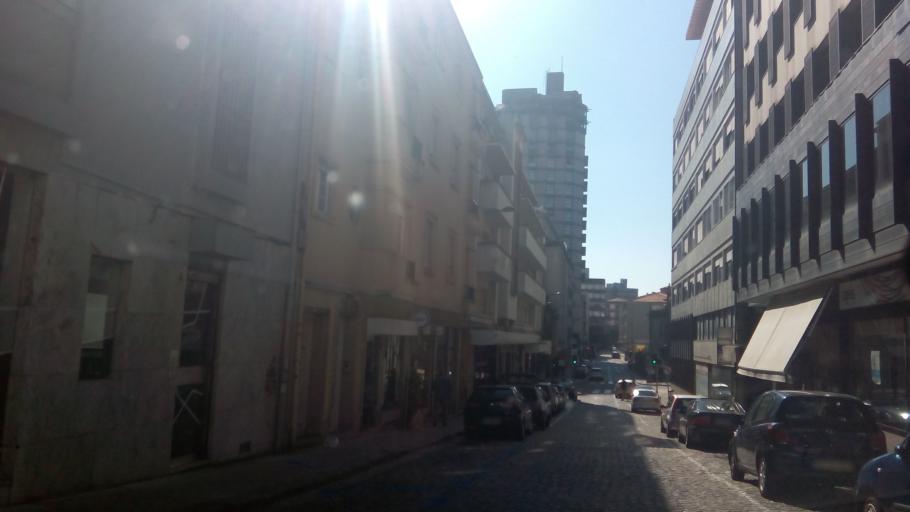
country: PT
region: Porto
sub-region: Porto
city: Porto
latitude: 41.1521
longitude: -8.6049
